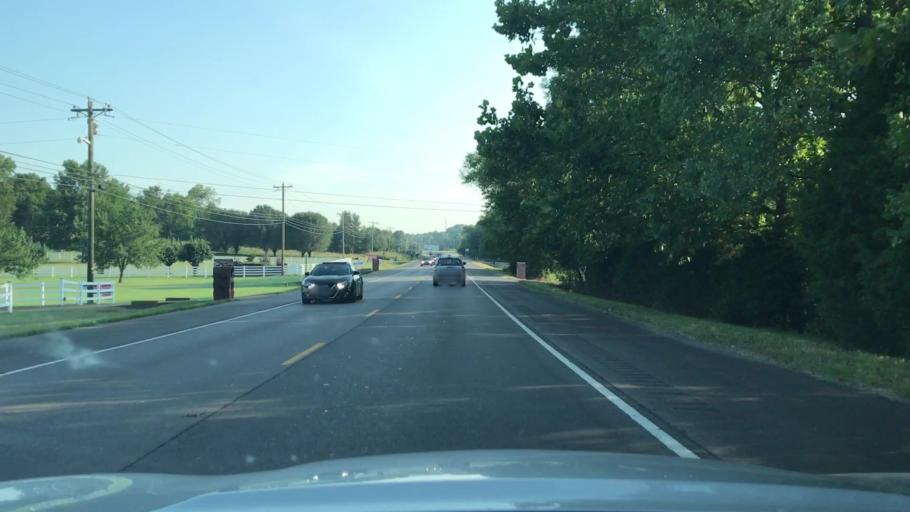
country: US
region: Tennessee
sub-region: Wilson County
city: Rural Hill
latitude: 36.1442
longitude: -86.5164
